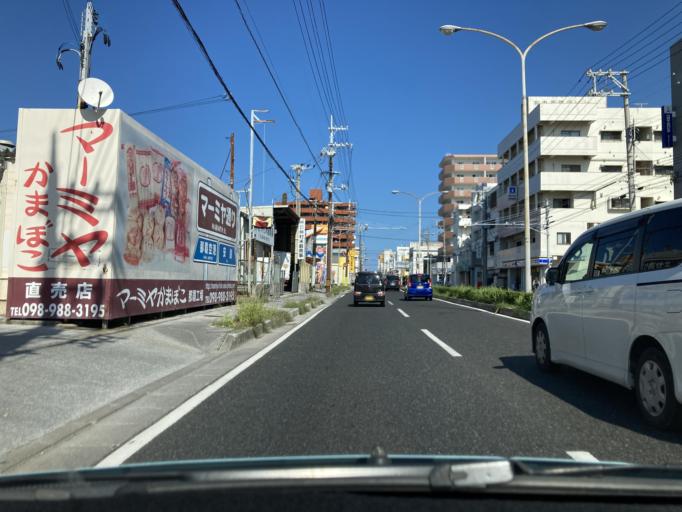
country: JP
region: Okinawa
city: Naha-shi
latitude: 26.2358
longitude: 127.6815
